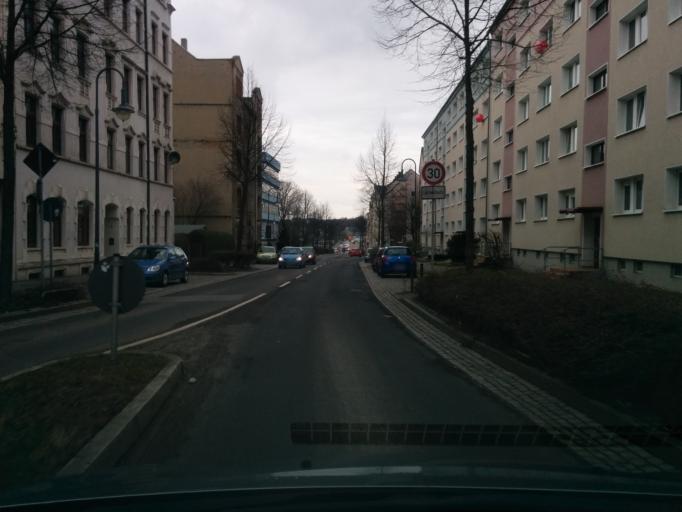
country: DE
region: Saxony
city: Chemnitz
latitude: 50.8394
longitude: 12.9417
